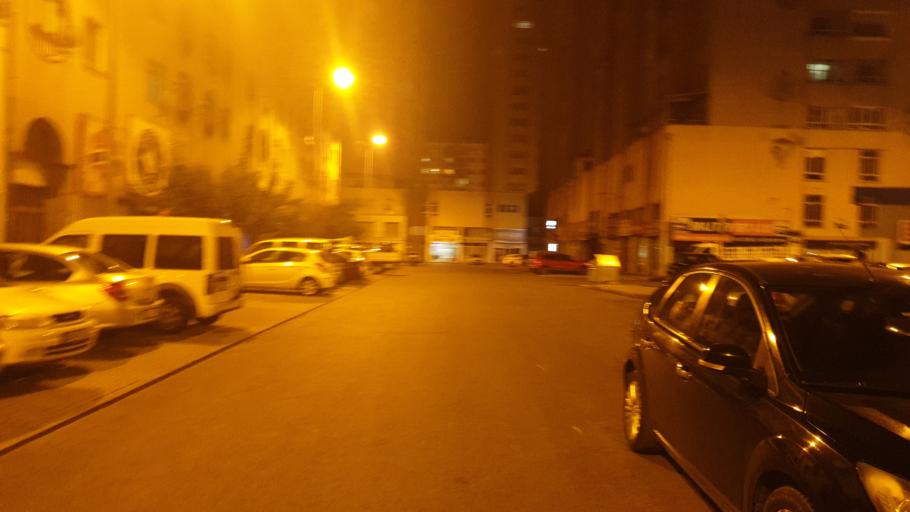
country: TR
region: Kayseri
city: Kayseri
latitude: 38.7290
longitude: 35.4951
